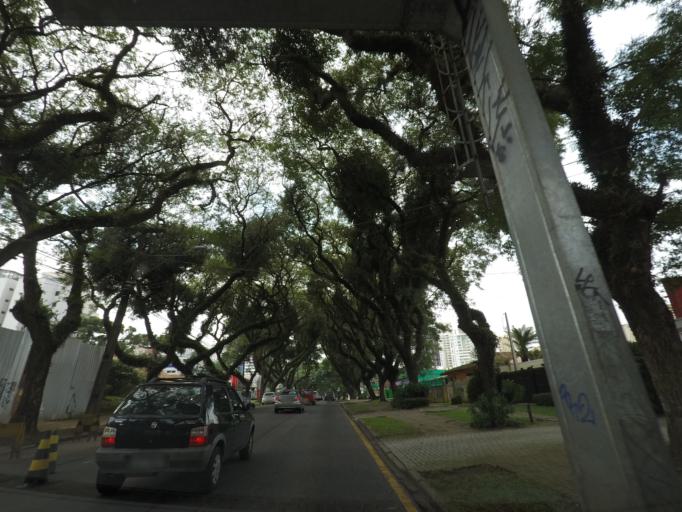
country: BR
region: Parana
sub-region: Curitiba
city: Curitiba
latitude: -25.4531
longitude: -49.2932
